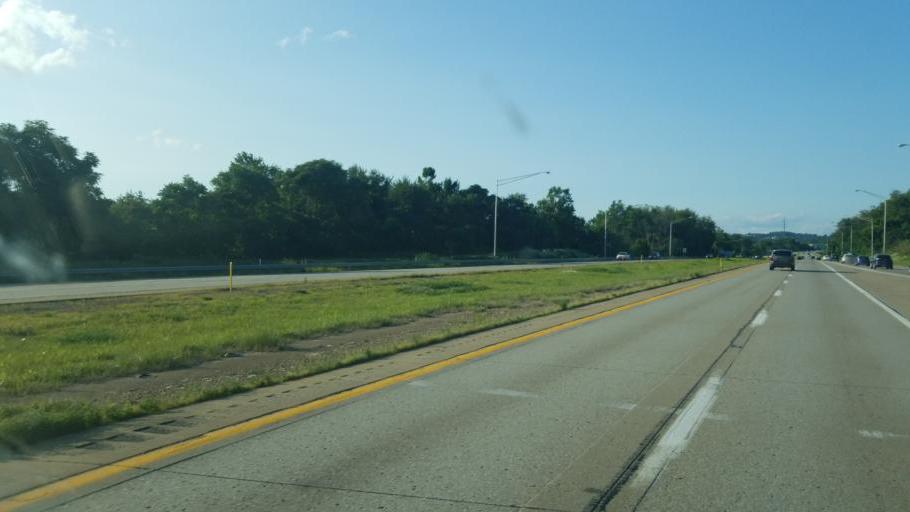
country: US
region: Pennsylvania
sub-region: Washington County
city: McGovern
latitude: 40.2243
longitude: -80.2128
